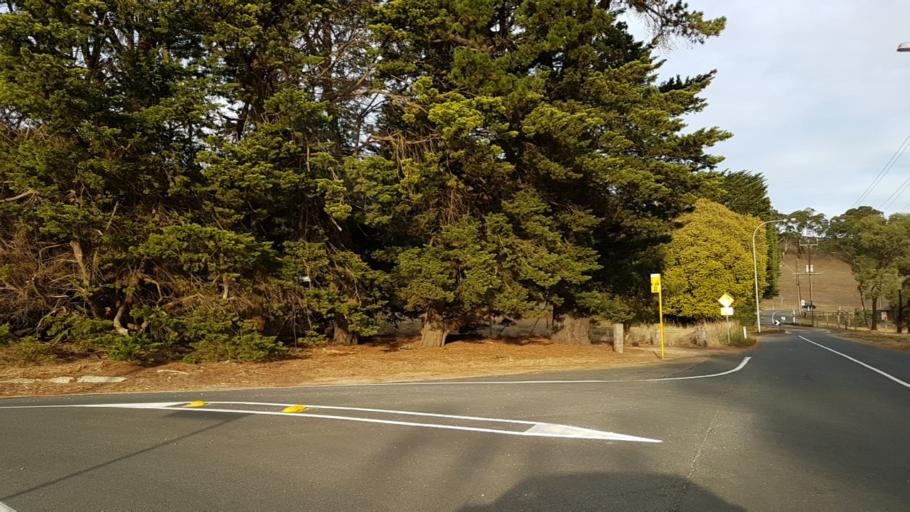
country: AU
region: South Australia
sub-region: Mount Barker
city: Nairne
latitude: -35.0237
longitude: 138.9085
